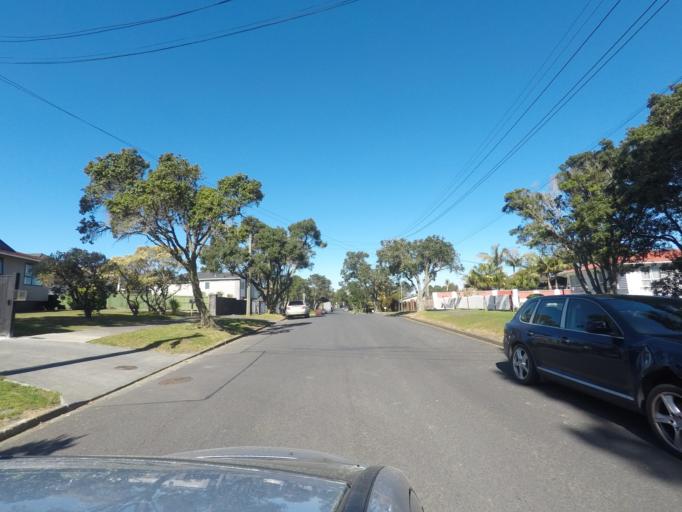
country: NZ
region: Auckland
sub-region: Auckland
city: Waitakere
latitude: -36.9270
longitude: 174.6947
